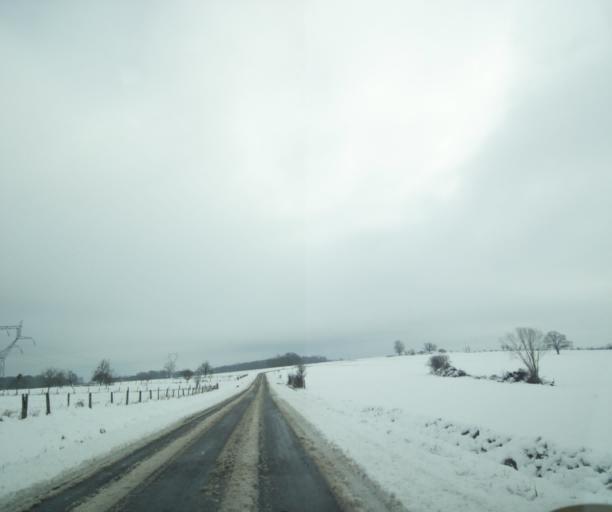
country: FR
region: Champagne-Ardenne
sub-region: Departement de la Haute-Marne
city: Montier-en-Der
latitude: 48.5074
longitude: 4.7280
